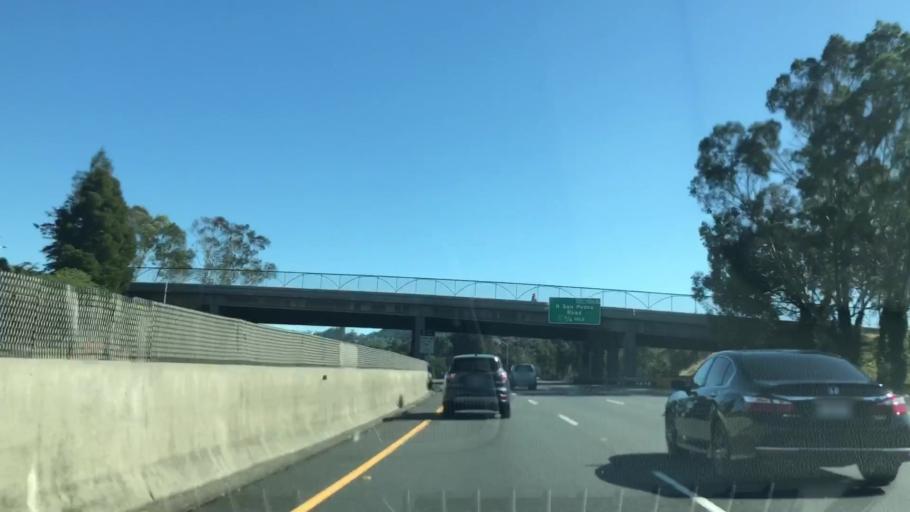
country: US
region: California
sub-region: Marin County
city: Santa Venetia
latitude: 38.0079
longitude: -122.5420
